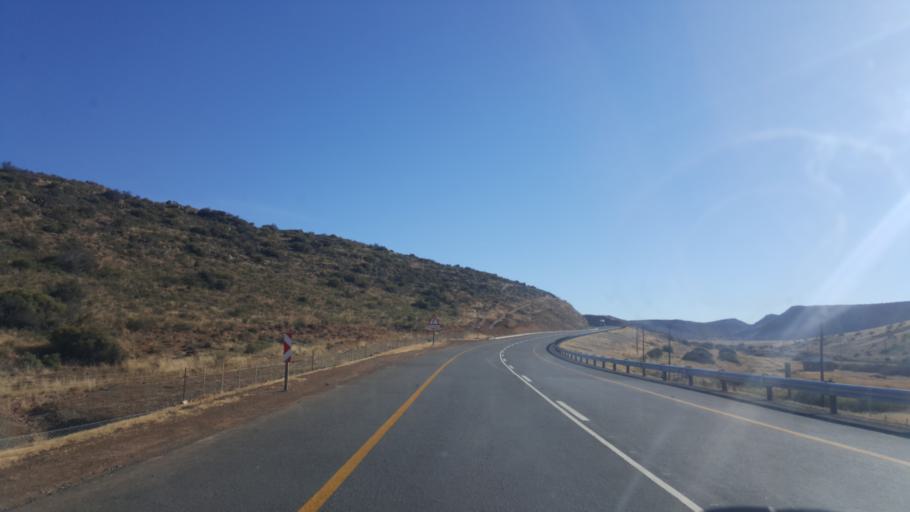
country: ZA
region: Eastern Cape
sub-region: Chris Hani District Municipality
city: Middelburg
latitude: -31.3837
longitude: 25.0322
